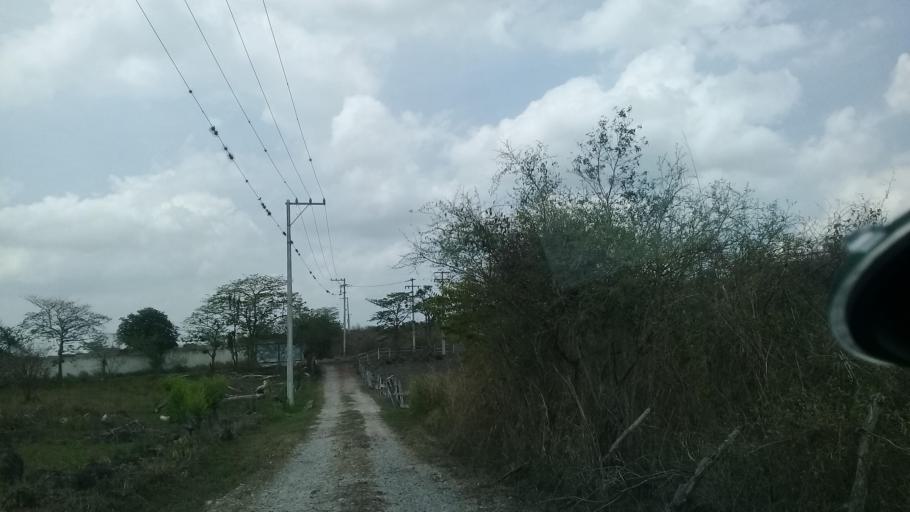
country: MX
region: Veracruz
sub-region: Emiliano Zapata
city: Plan del Rio
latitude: 19.4276
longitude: -96.6940
